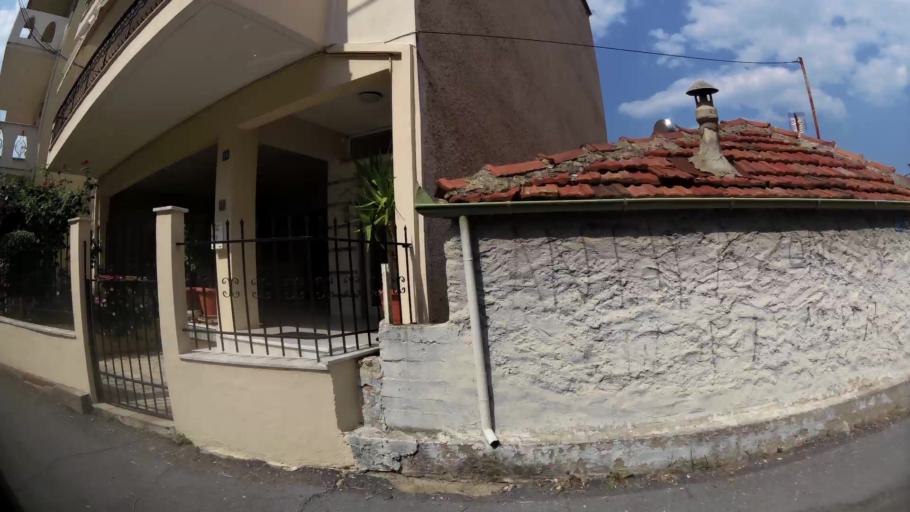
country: GR
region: Central Macedonia
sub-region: Nomos Imathias
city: Veroia
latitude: 40.5156
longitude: 22.2074
